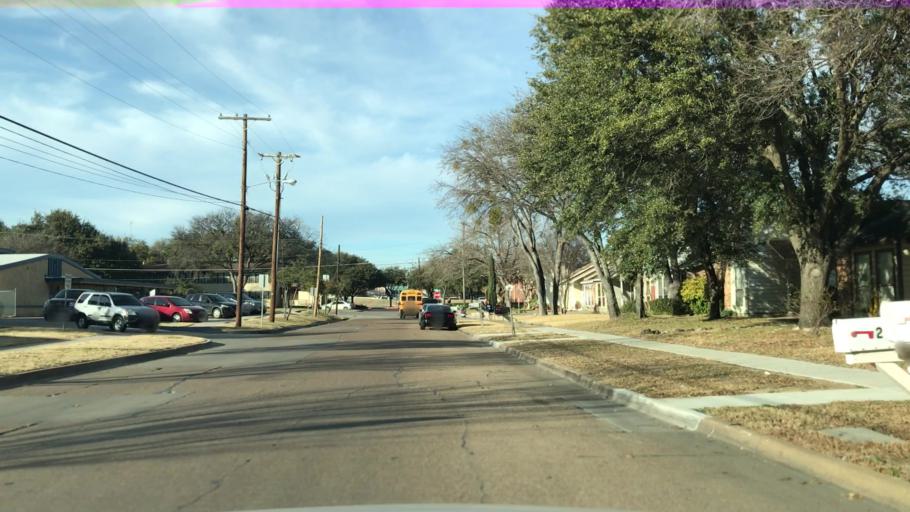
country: US
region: Texas
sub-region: Dallas County
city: Irving
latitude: 32.8114
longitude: -96.9580
